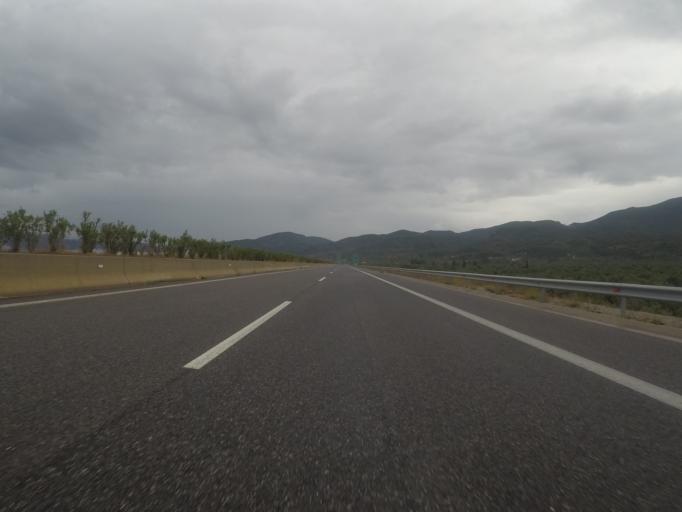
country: GR
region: Peloponnese
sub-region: Nomos Messinias
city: Meligalas
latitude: 37.2379
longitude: 22.0167
